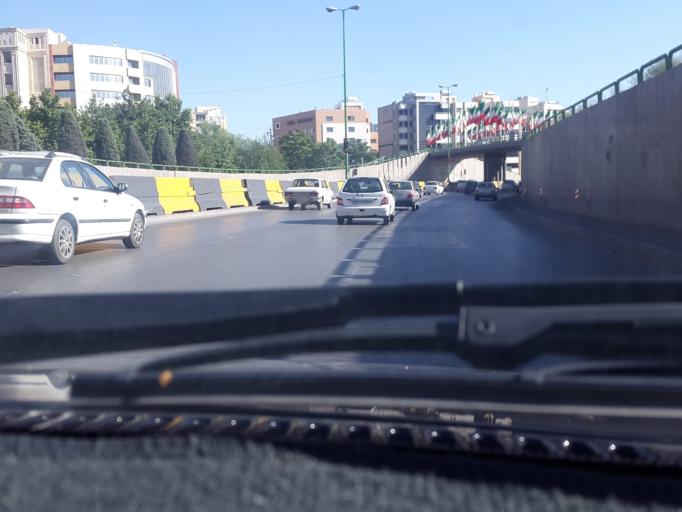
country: IR
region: Isfahan
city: Isfahan
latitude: 32.6475
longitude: 51.6434
